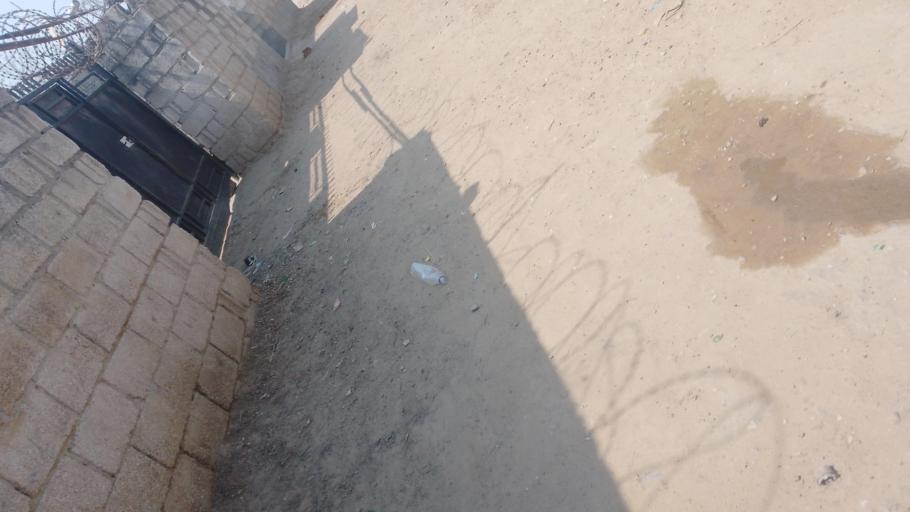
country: ZM
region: Lusaka
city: Lusaka
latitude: -15.4074
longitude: 28.3778
